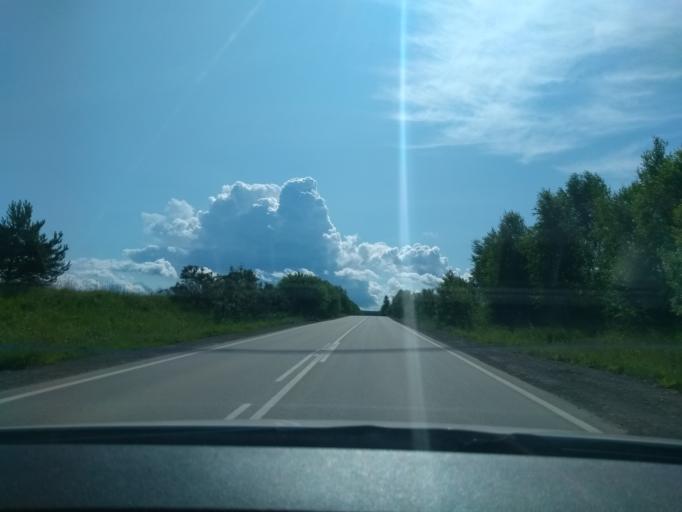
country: RU
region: Perm
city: Bershet'
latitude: 57.8153
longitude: 56.4476
